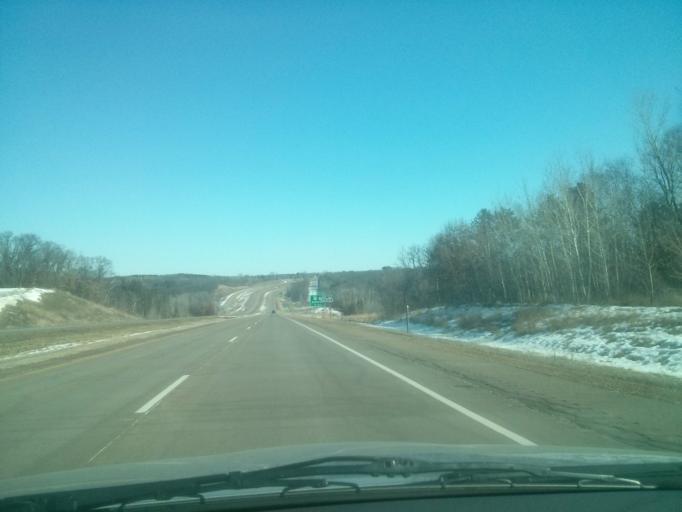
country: US
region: Wisconsin
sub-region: Saint Croix County
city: Somerset
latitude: 45.0949
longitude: -92.7361
